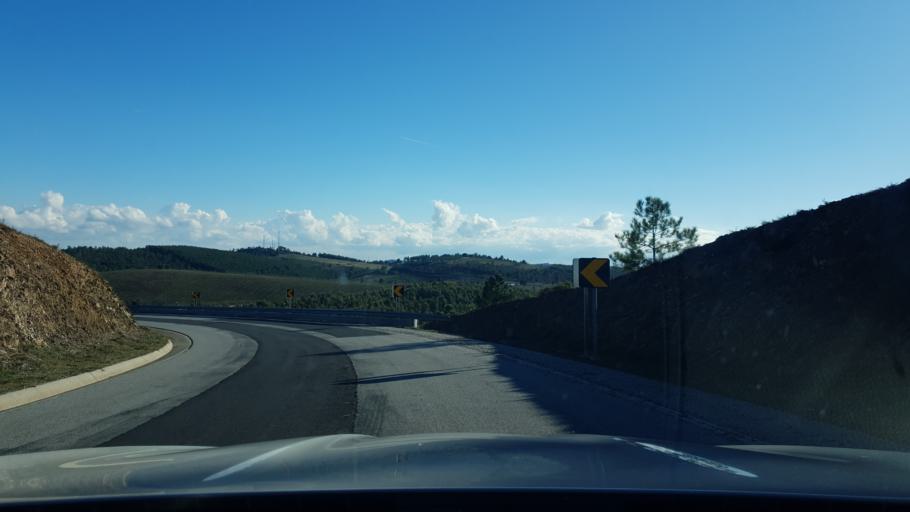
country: PT
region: Braganca
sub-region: Freixo de Espada A Cinta
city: Freixo de Espada a Cinta
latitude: 41.1293
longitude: -6.8193
